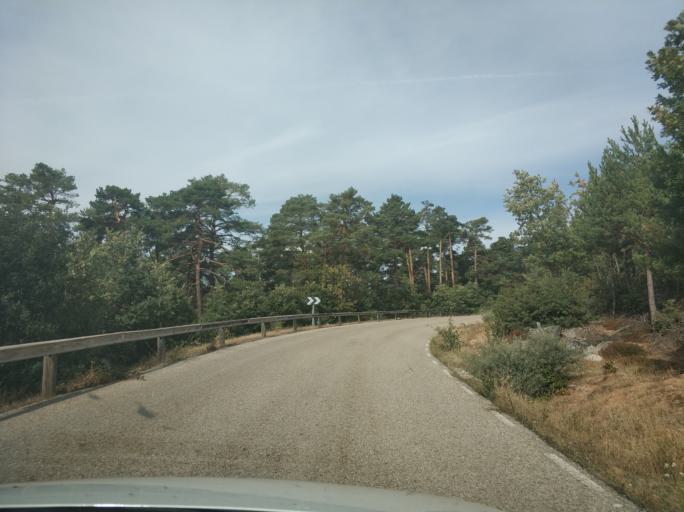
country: ES
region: Castille and Leon
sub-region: Provincia de Soria
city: Duruelo de la Sierra
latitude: 41.9079
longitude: -2.9457
